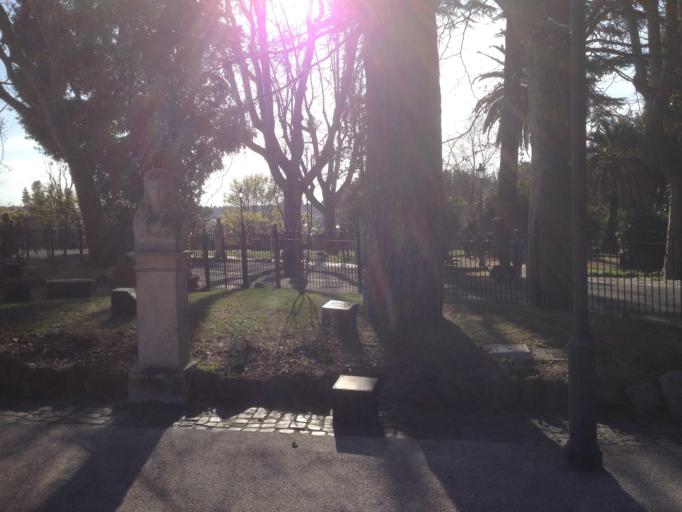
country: VA
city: Vatican City
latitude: 41.9105
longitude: 12.4798
